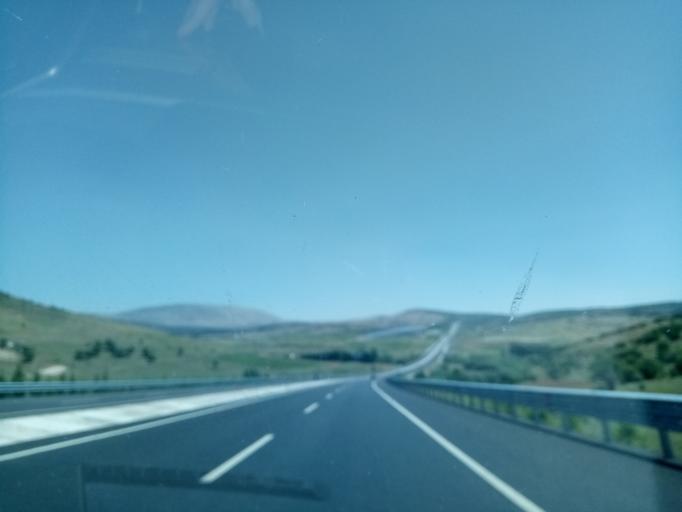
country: TR
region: Konya
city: Kiziloren
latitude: 37.7579
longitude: 32.2130
